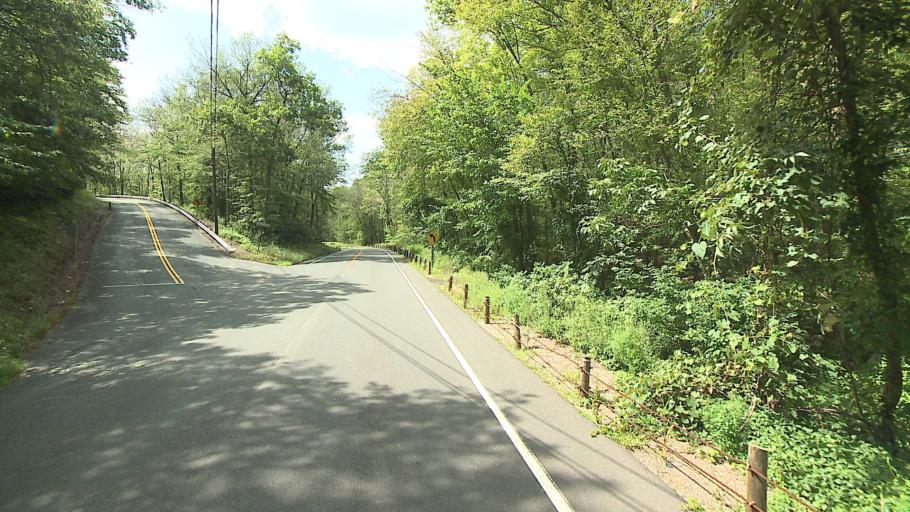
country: US
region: Connecticut
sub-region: Tolland County
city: Ellington
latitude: 41.9144
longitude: -72.4320
